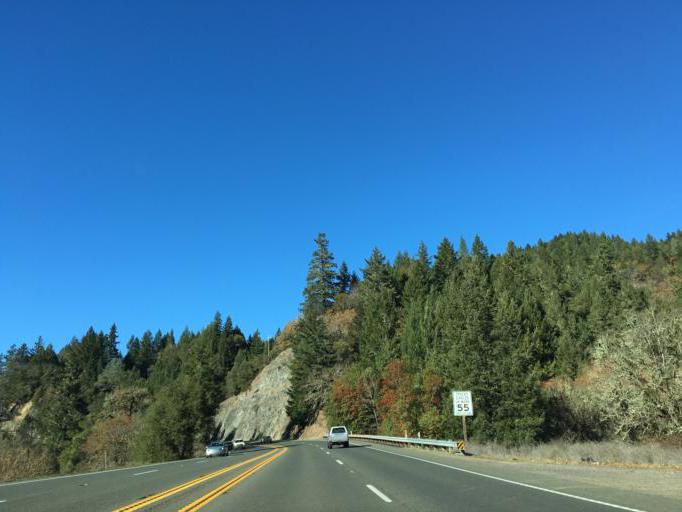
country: US
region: California
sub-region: Mendocino County
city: Brooktrails
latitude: 39.5207
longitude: -123.3925
